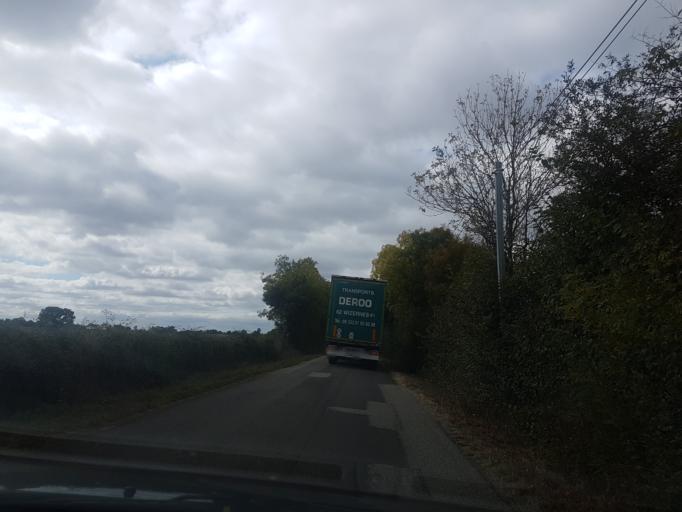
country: FR
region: Pays de la Loire
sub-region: Departement de la Loire-Atlantique
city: Ligne
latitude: 47.4007
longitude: -1.3948
